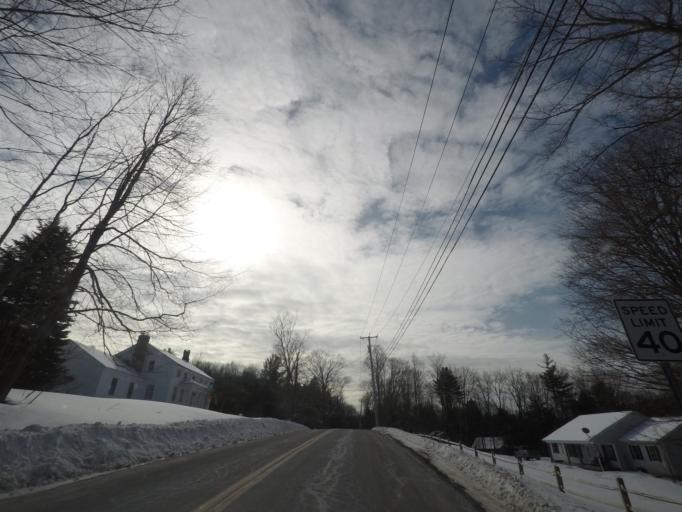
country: US
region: New York
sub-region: Rensselaer County
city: Averill Park
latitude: 42.5833
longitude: -73.4875
